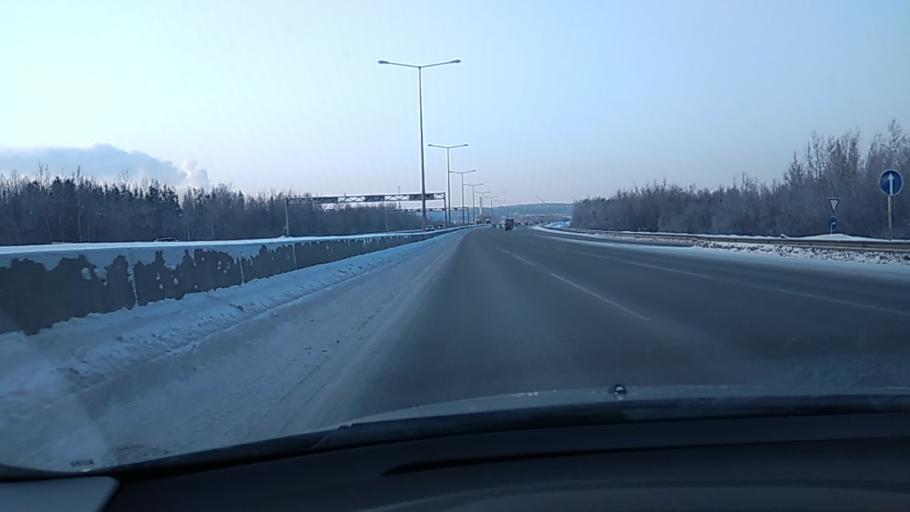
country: RU
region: Sverdlovsk
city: Istok
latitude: 56.7621
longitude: 60.7627
